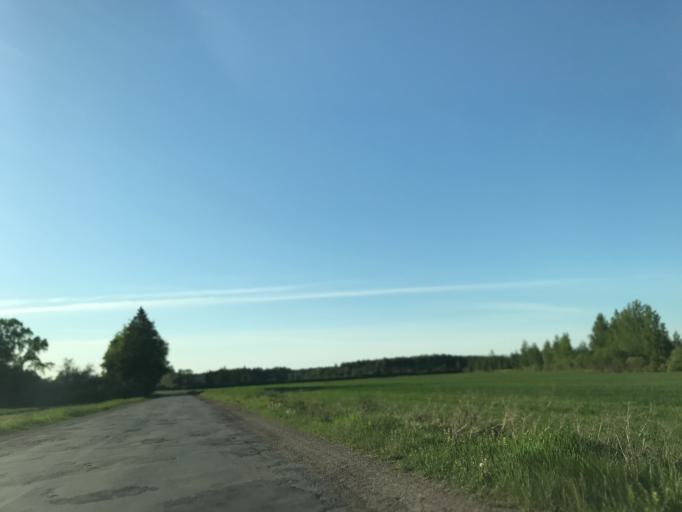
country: LV
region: Ozolnieku
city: Ozolnieki
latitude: 56.5799
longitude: 23.8263
